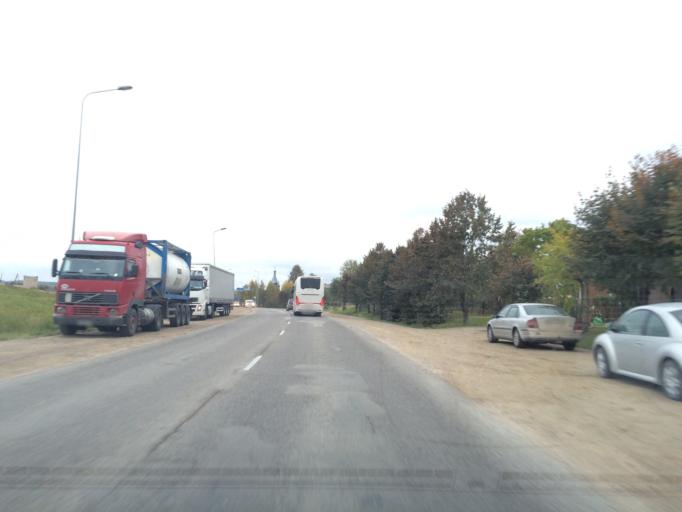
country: LV
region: Jekabpils Rajons
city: Jekabpils
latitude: 56.5054
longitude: 25.8841
